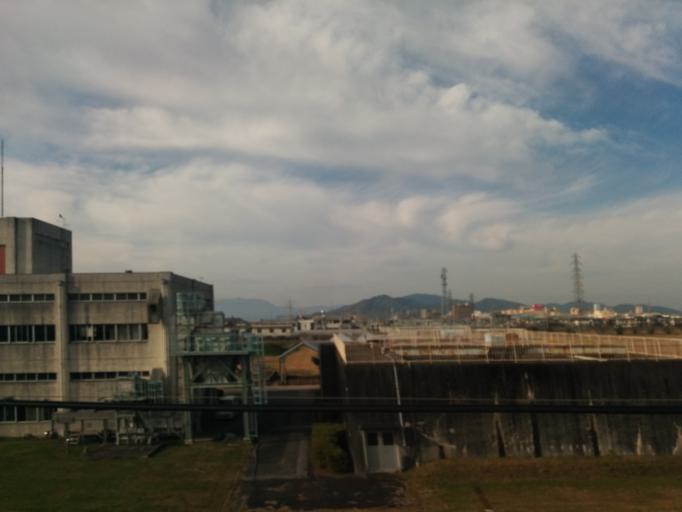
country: JP
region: Shiga Prefecture
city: Omihachiman
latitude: 35.1087
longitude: 136.1083
